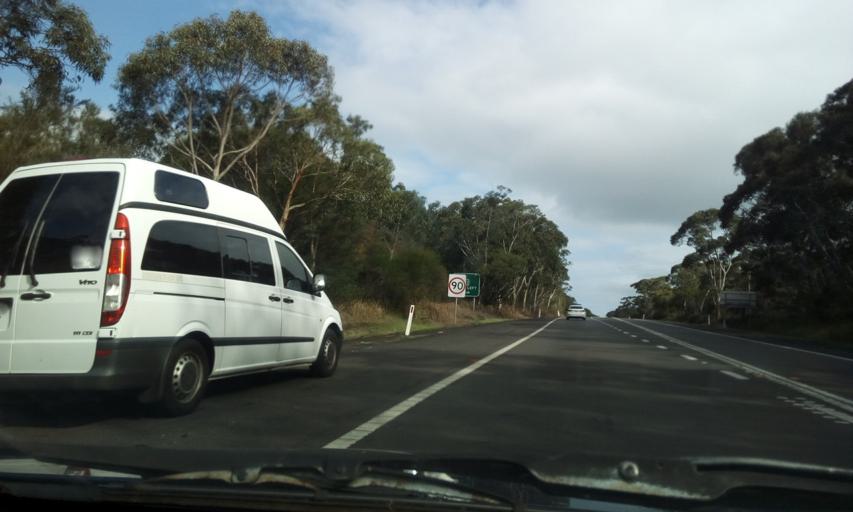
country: AU
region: New South Wales
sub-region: Wollongong
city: Bulli
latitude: -34.2865
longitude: 150.9008
